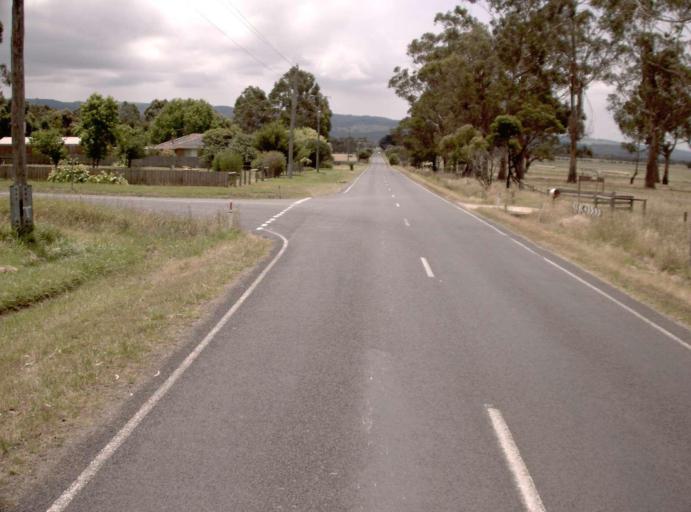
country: AU
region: Victoria
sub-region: Latrobe
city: Traralgon
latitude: -38.5295
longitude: 146.6590
